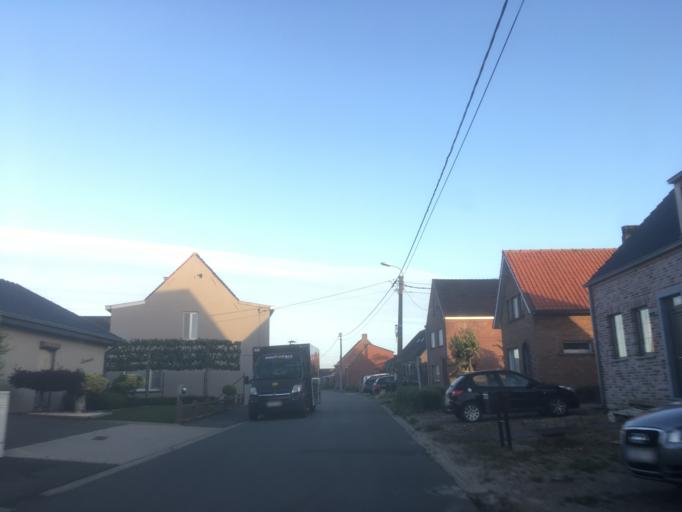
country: BE
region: Flanders
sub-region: Provincie West-Vlaanderen
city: Hooglede
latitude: 51.0212
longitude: 3.0942
